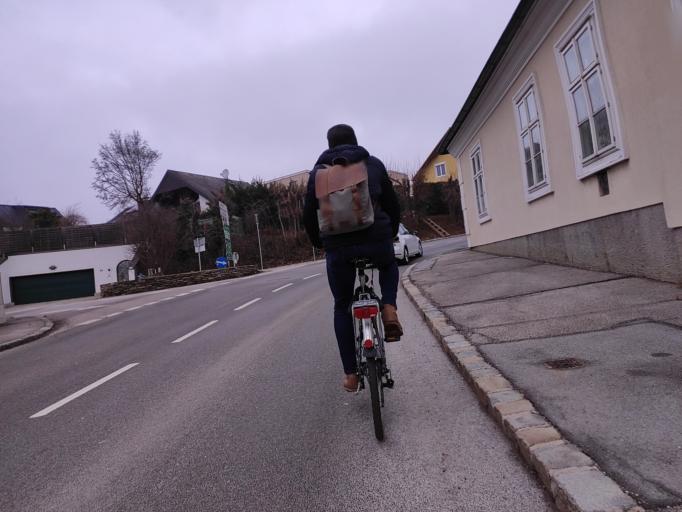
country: AT
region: Lower Austria
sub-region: Politischer Bezirk Modling
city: Hinterbruehl
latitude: 48.0944
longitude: 16.2602
